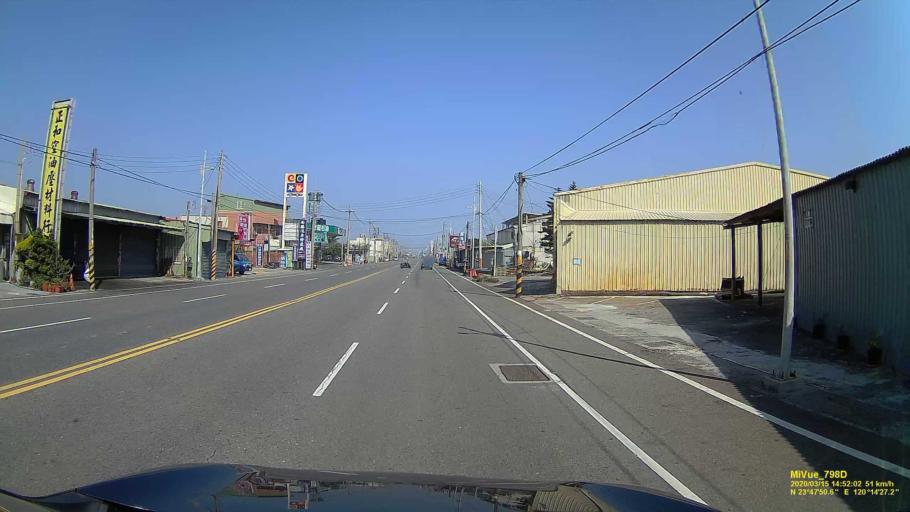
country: TW
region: Taiwan
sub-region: Yunlin
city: Douliu
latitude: 23.7974
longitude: 120.2410
